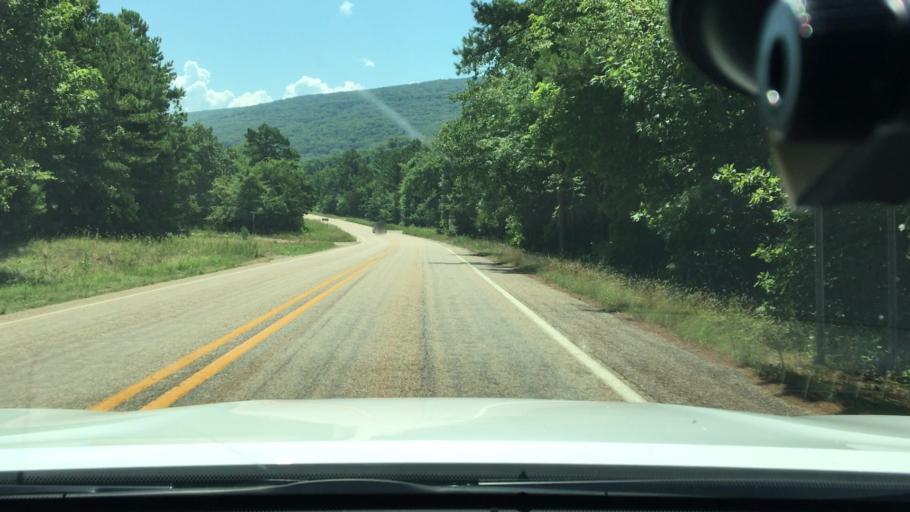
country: US
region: Arkansas
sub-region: Logan County
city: Paris
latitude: 35.1946
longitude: -93.6316
